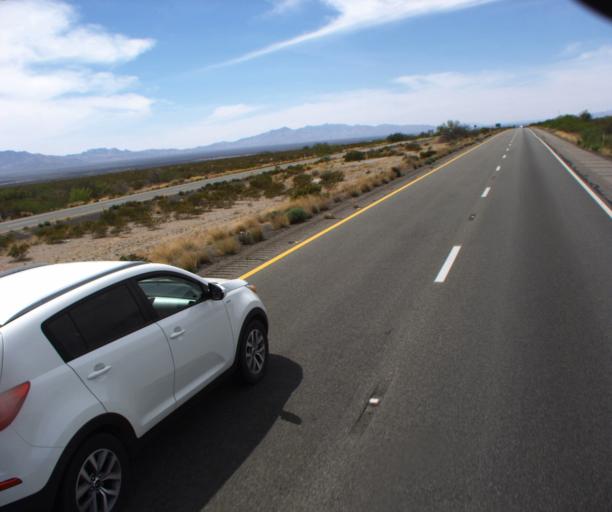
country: US
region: New Mexico
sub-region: Hidalgo County
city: Lordsburg
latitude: 32.2412
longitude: -109.1074
